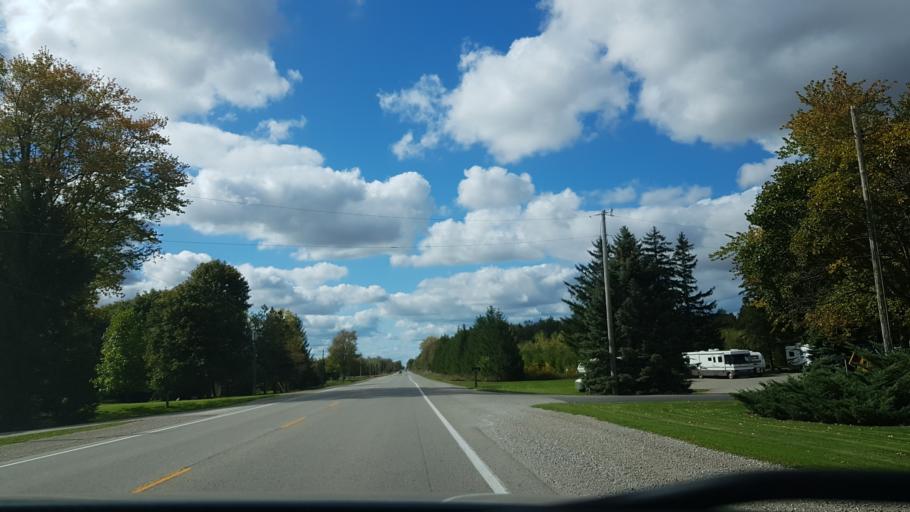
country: CA
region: Ontario
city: South Huron
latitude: 43.3576
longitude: -81.5233
